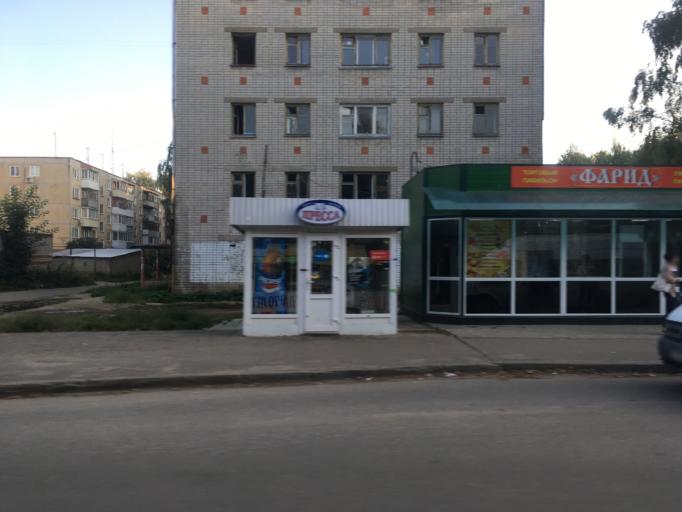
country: RU
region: Mariy-El
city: Yoshkar-Ola
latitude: 56.6488
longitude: 47.8762
